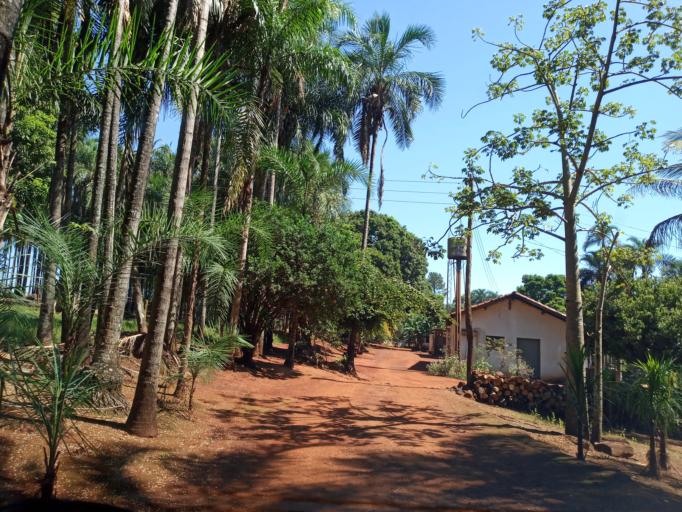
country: BR
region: Goias
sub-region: Itumbiara
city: Itumbiara
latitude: -18.4398
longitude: -49.1437
